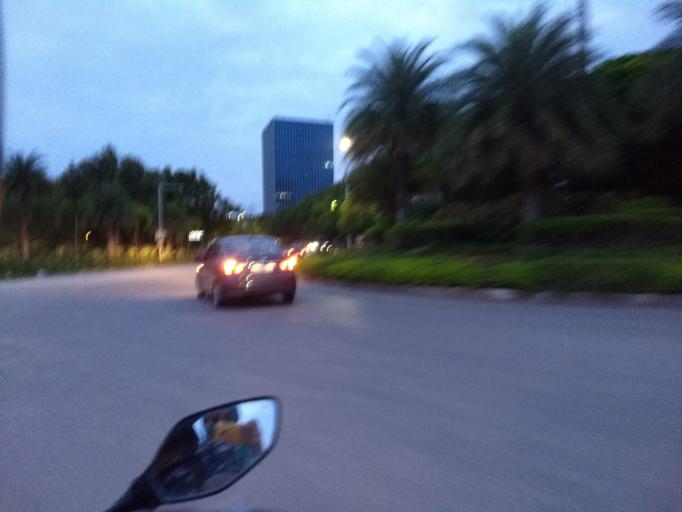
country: IN
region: Telangana
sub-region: Rangareddi
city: Kukatpalli
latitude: 17.4089
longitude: 78.3726
